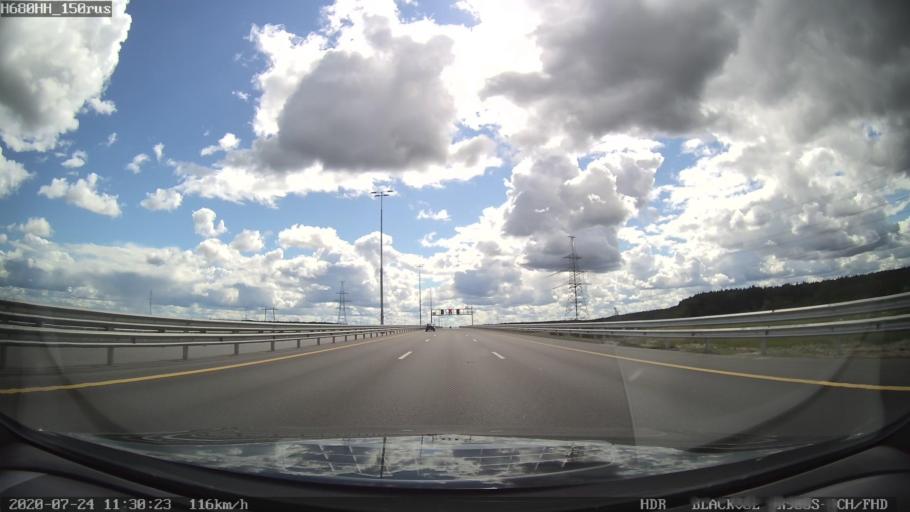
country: RU
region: Leningrad
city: Krasnyy Bor
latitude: 59.6702
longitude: 30.6116
